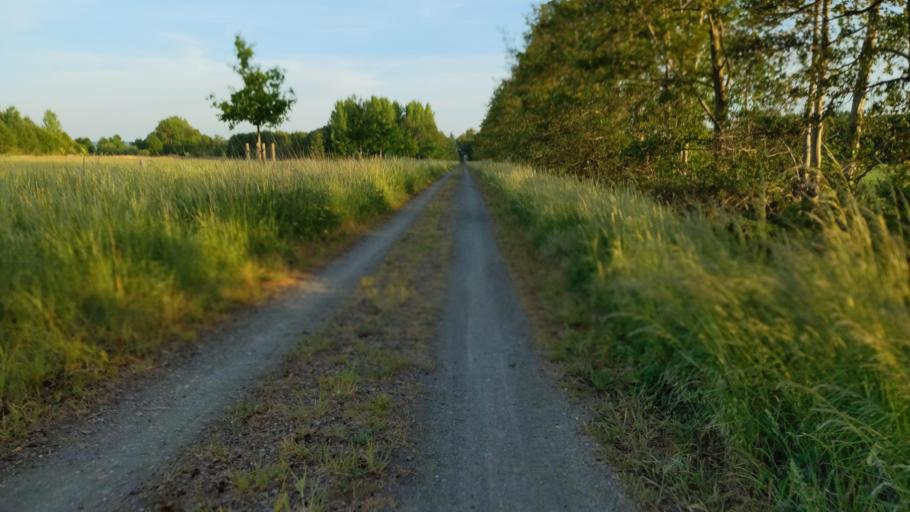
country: DE
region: Lower Saxony
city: Sickte
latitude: 52.2263
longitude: 10.5958
